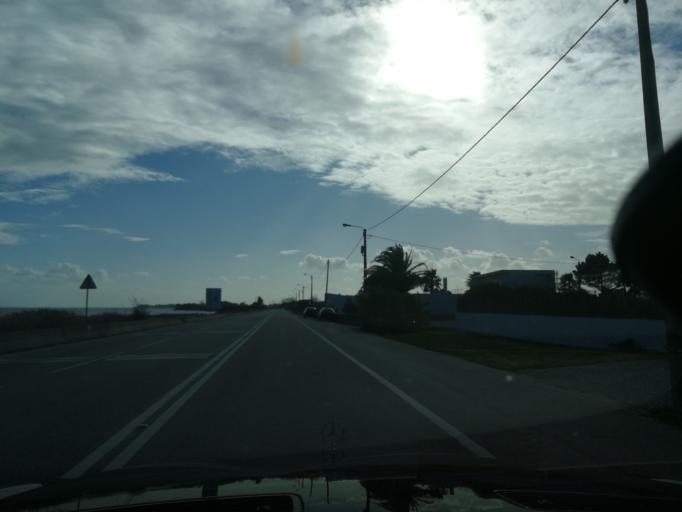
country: PT
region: Aveiro
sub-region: Murtosa
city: Murtosa
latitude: 40.7746
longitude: -8.6931
